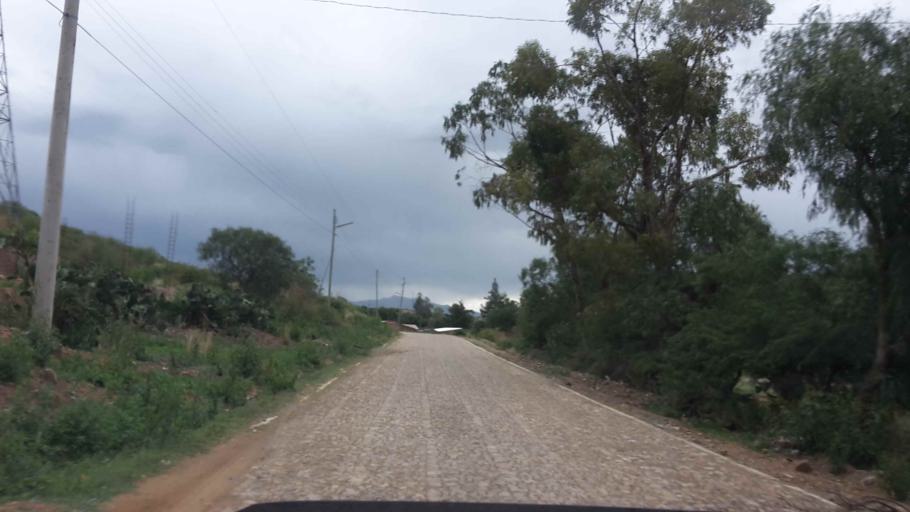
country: BO
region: Cochabamba
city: Cochabamba
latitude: -17.5431
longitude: -66.1922
